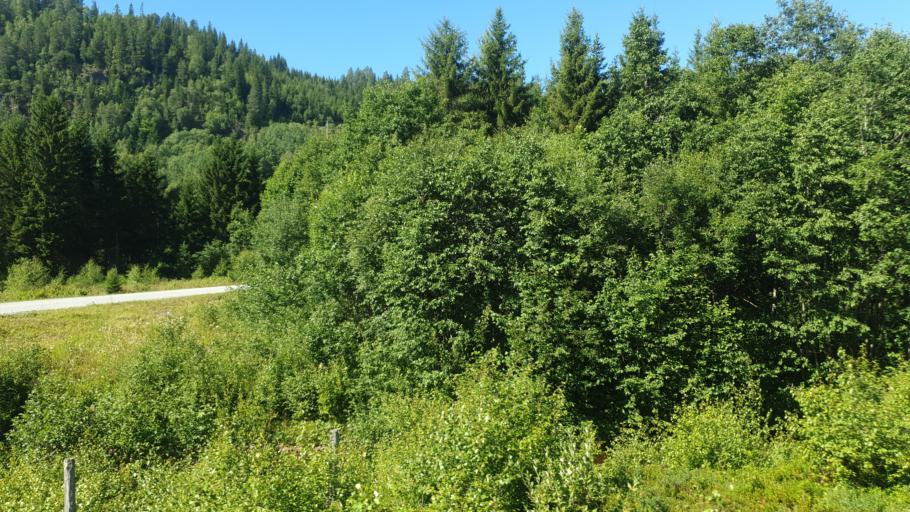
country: NO
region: Sor-Trondelag
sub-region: Meldal
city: Meldal
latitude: 63.1441
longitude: 9.7142
